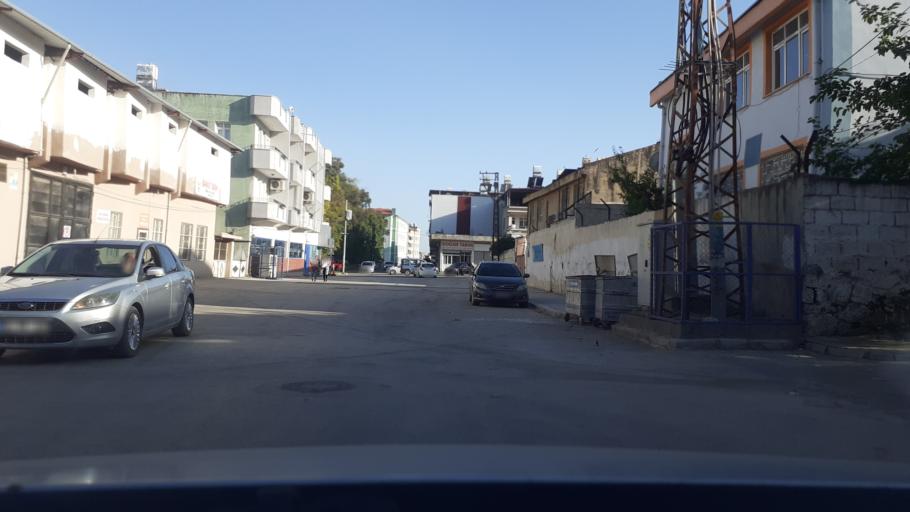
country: TR
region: Hatay
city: Kirikhan
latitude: 36.5000
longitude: 36.3651
